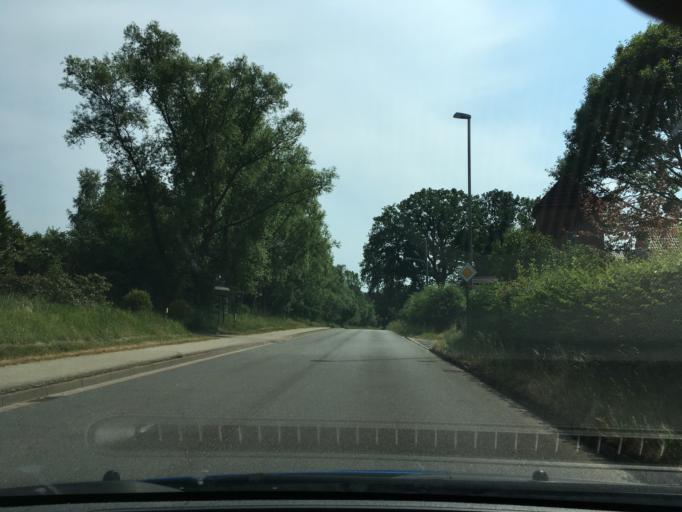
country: DE
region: Lower Saxony
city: Buchholz in der Nordheide
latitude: 53.3132
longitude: 9.9075
